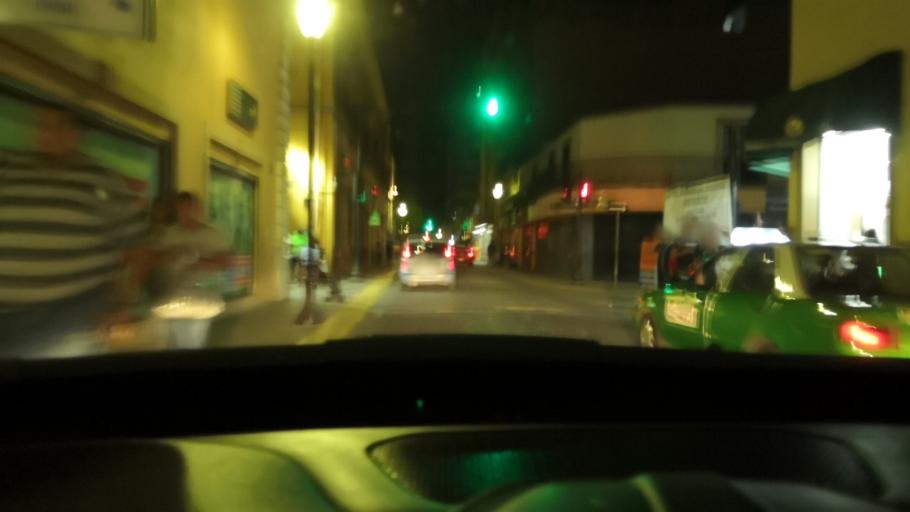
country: MX
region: Guanajuato
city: Leon
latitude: 21.1216
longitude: -101.6836
